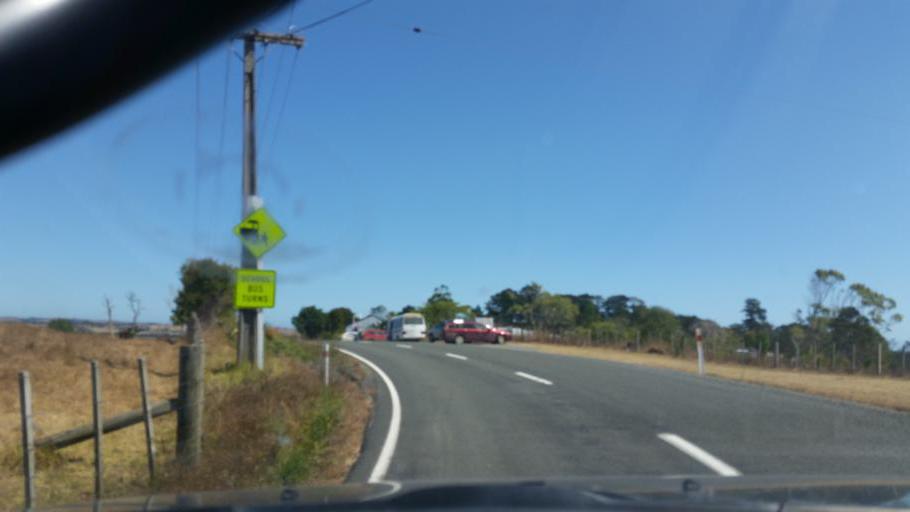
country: NZ
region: Northland
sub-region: Kaipara District
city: Dargaville
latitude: -36.0070
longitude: 173.9460
